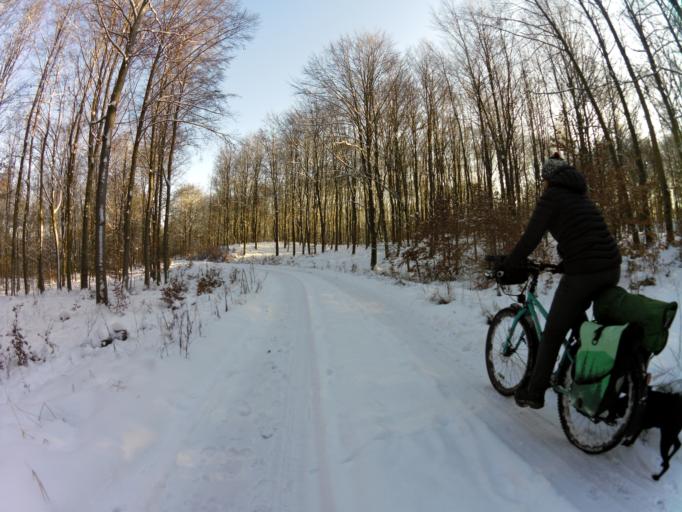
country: PL
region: West Pomeranian Voivodeship
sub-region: Powiat stargardzki
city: Insko
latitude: 53.3918
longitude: 15.5422
